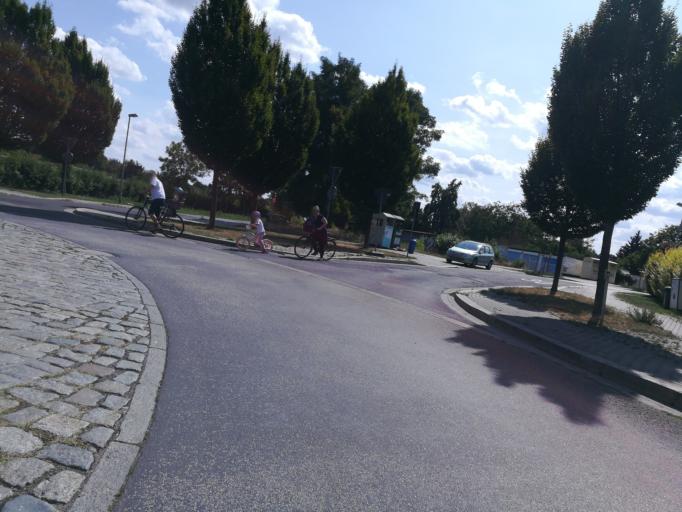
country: DE
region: Saxony-Anhalt
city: Neue Neustadt
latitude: 52.1479
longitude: 11.6133
